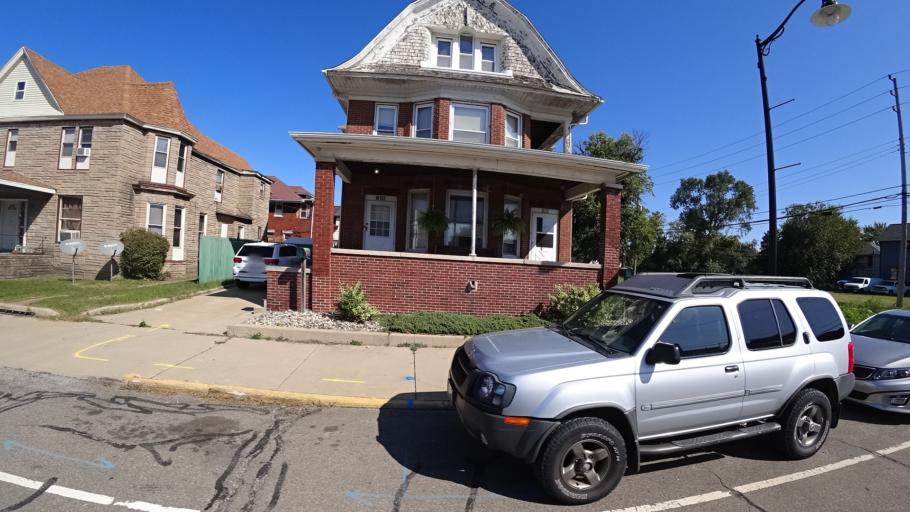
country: US
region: Indiana
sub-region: LaPorte County
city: Michigan City
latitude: 41.7140
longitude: -86.8985
